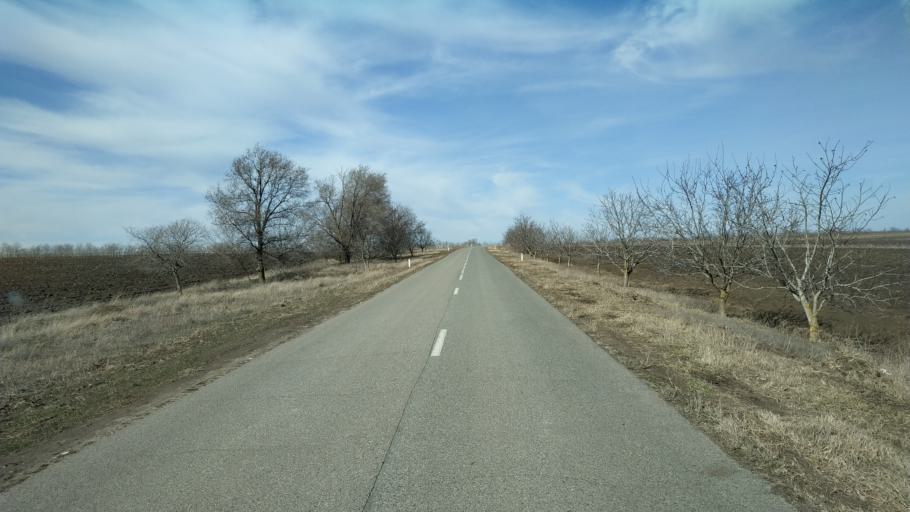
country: MD
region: Nisporeni
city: Nisporeni
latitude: 46.9402
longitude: 28.2455
